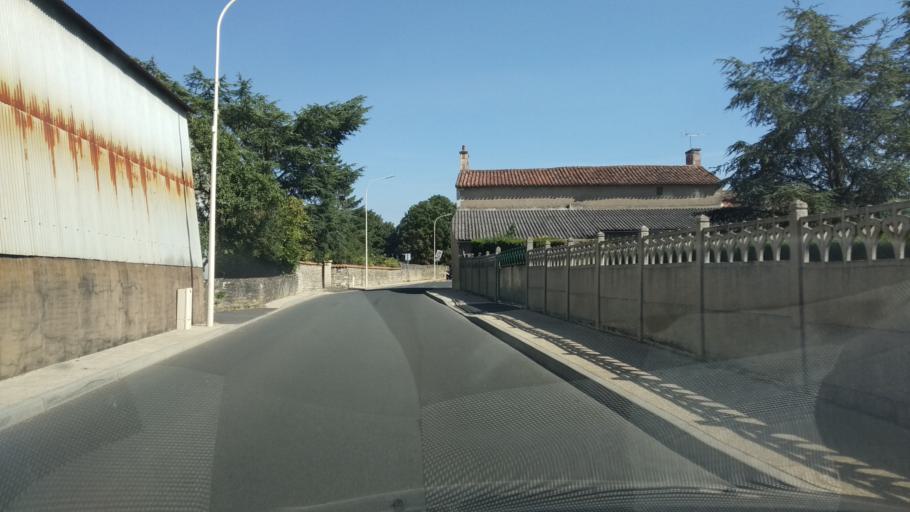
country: FR
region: Poitou-Charentes
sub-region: Departement de la Vienne
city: Cisse
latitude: 46.6459
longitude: 0.2296
